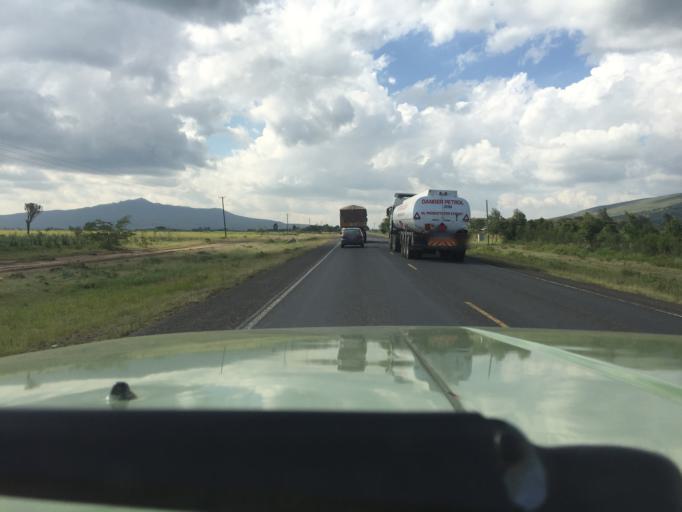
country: KE
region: Nakuru
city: Kijabe
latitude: -0.9574
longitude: 36.5559
